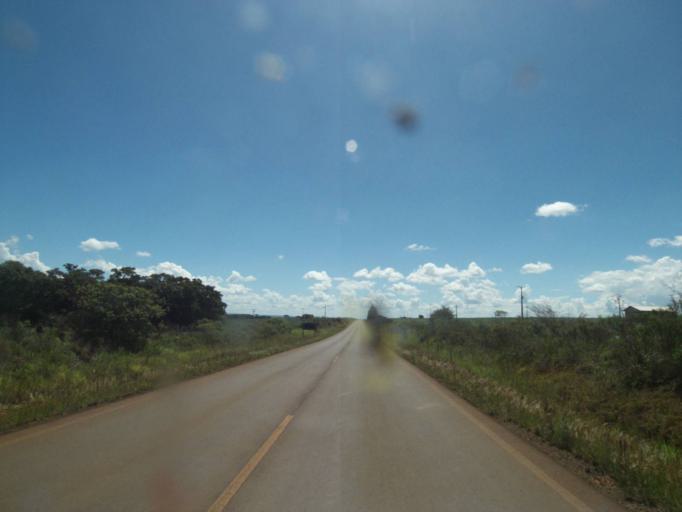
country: BR
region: Parana
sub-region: Pinhao
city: Pinhao
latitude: -25.8133
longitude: -52.0492
